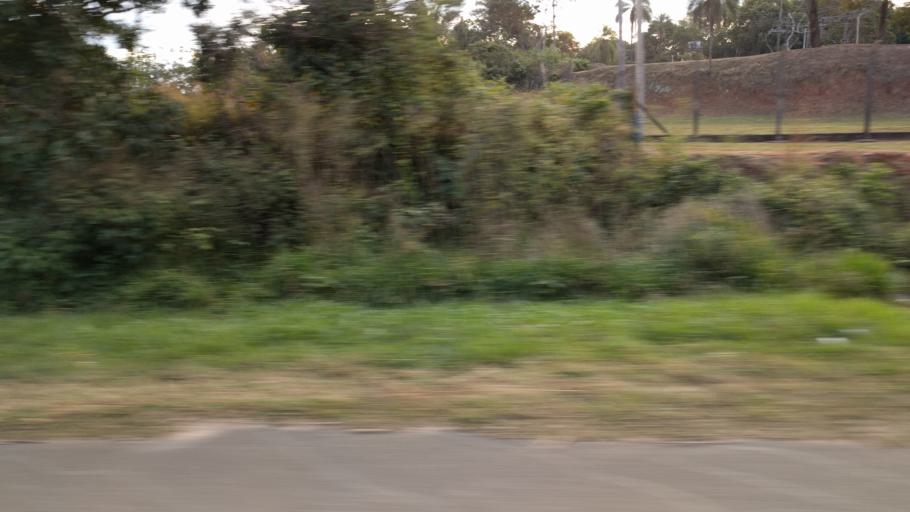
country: BO
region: Santa Cruz
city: Buena Vista
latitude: -17.4476
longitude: -63.6502
